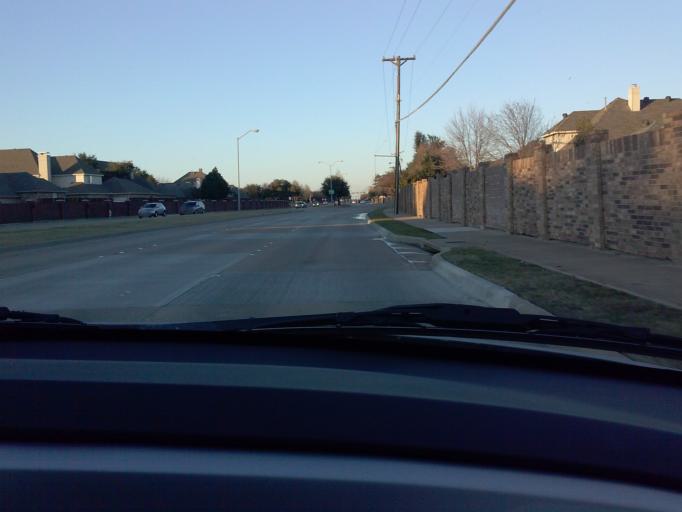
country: US
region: Texas
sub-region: Collin County
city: Plano
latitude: 33.0769
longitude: -96.7501
